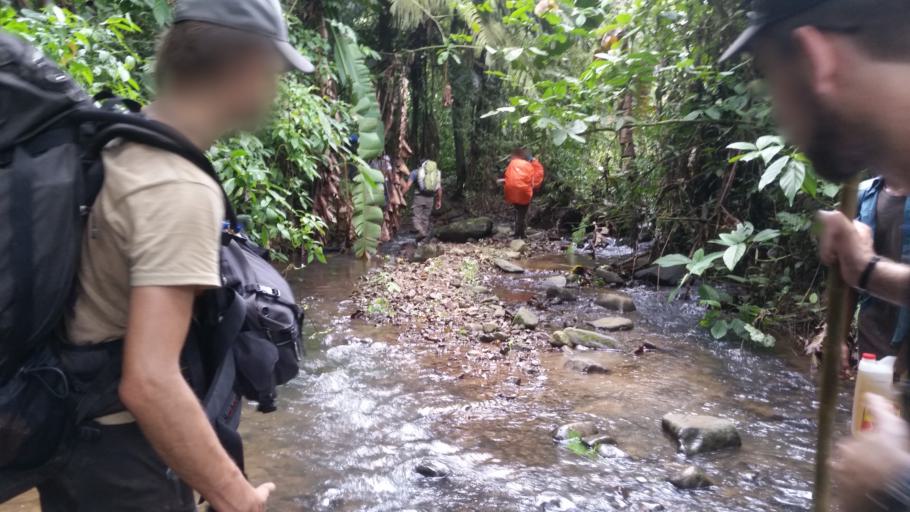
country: NI
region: Atlantico Norte (RAAN)
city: Bonanza
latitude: 14.0590
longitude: -84.7128
